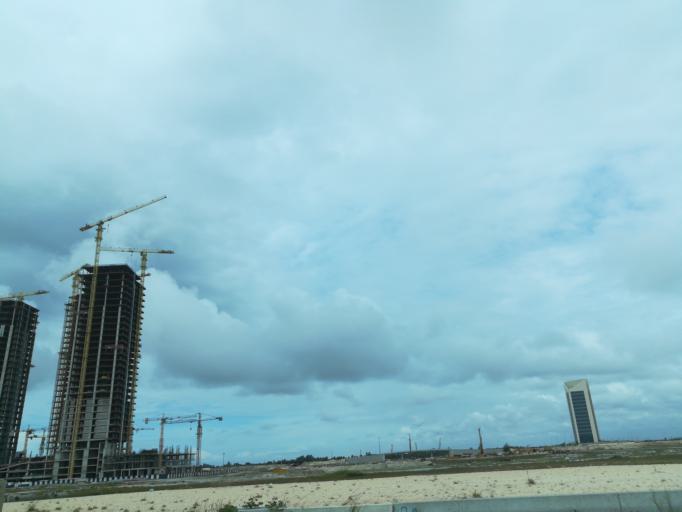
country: NG
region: Lagos
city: Lagos
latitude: 6.4044
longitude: 3.4098
